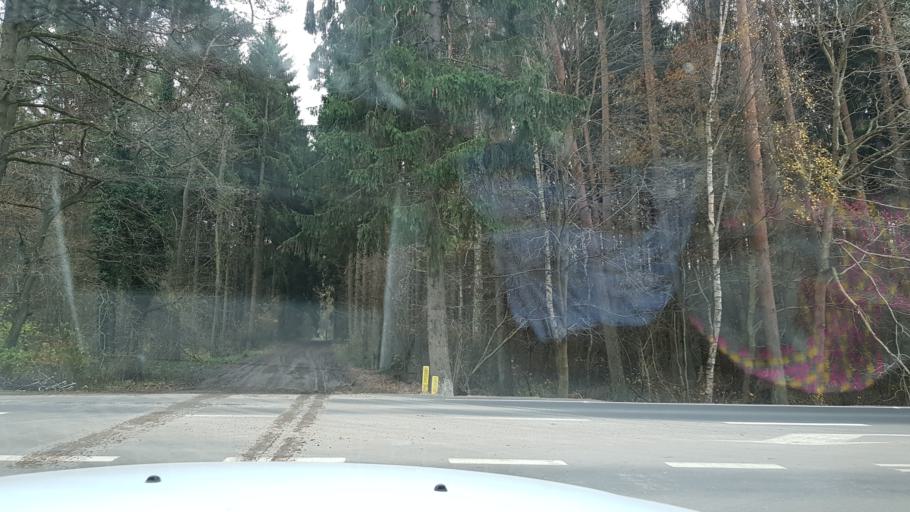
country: PL
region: West Pomeranian Voivodeship
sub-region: Powiat gryficki
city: Pobierowo
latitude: 54.0664
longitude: 14.9702
